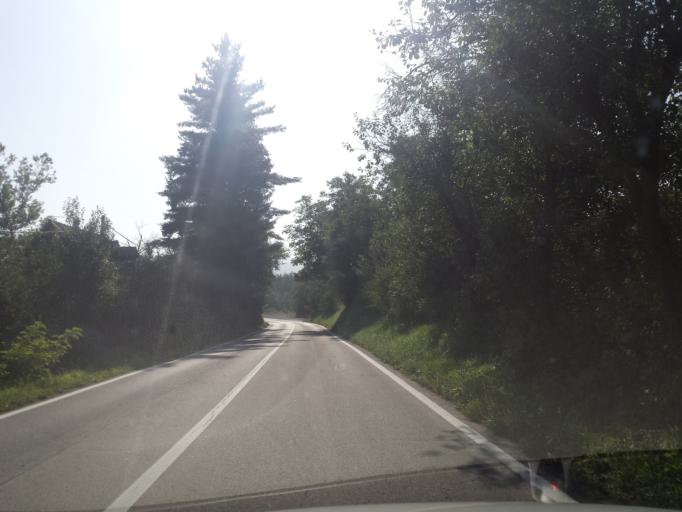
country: HR
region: Karlovacka
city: Ostarije
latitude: 45.2656
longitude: 15.3436
